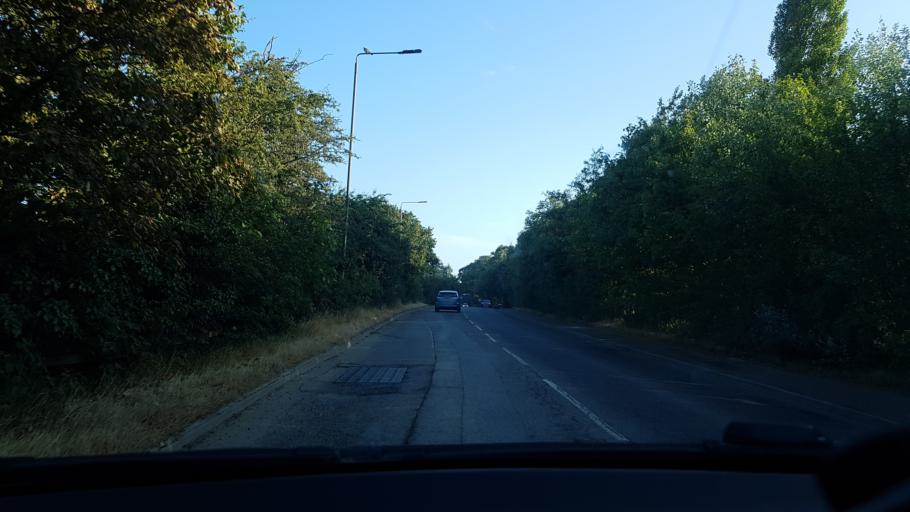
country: GB
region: England
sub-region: Derbyshire
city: Ilkeston
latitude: 52.9557
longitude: -1.3077
